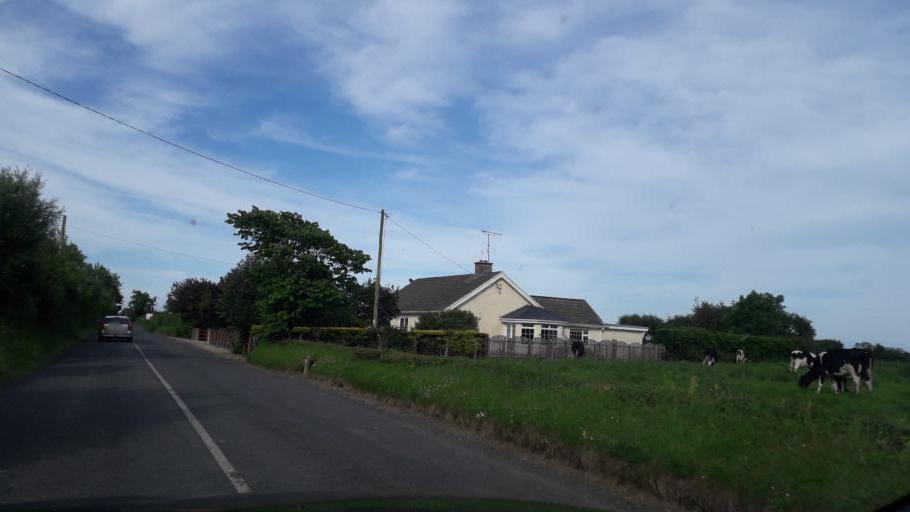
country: IE
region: Leinster
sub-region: Loch Garman
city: Courtown
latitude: 52.5522
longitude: -6.2463
